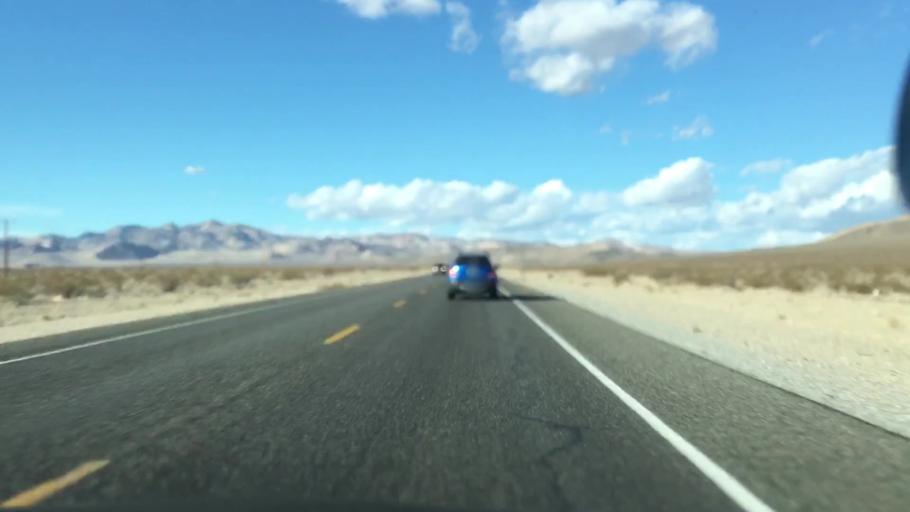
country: US
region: Nevada
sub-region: Nye County
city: Beatty
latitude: 36.8326
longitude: -116.7477
